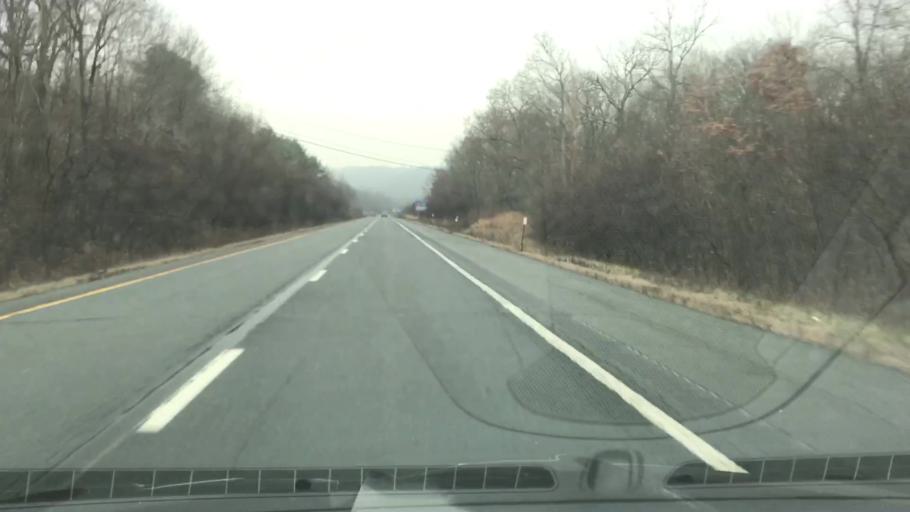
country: US
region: New York
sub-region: Orange County
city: Port Jervis
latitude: 41.3579
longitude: -74.6663
